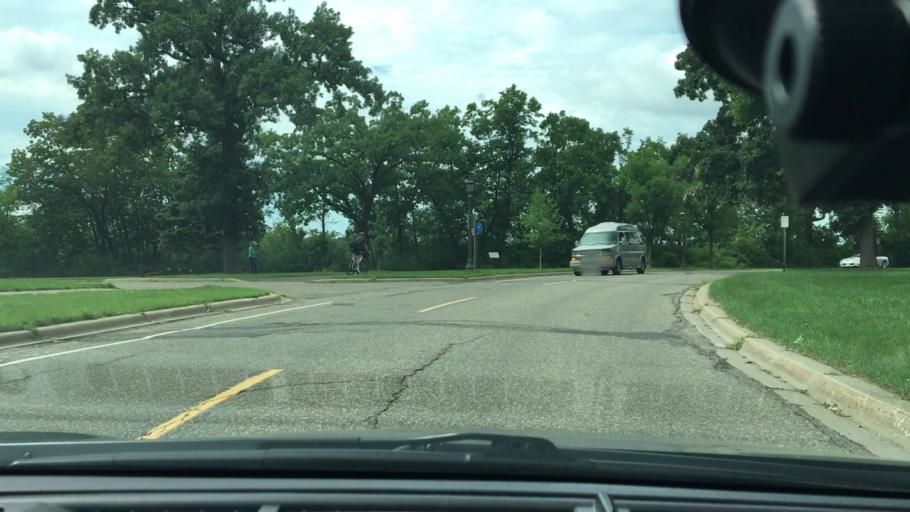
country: US
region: Minnesota
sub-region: Dakota County
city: Mendota Heights
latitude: 44.9225
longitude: -93.1976
